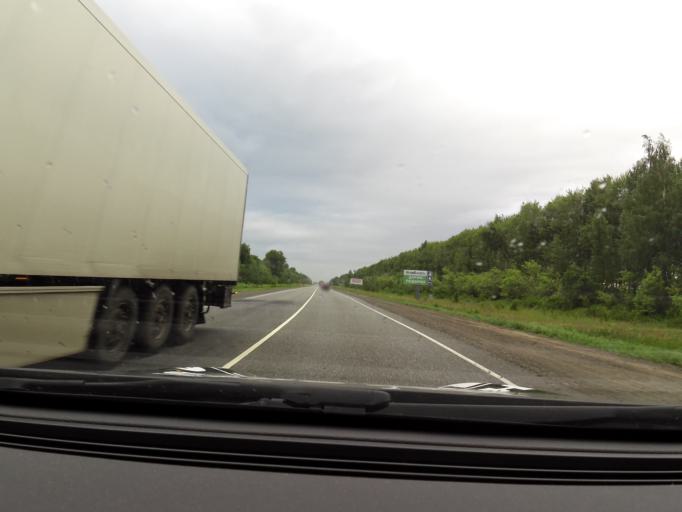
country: RU
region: Chuvashia
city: Kozlovka
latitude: 55.7978
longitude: 48.1207
